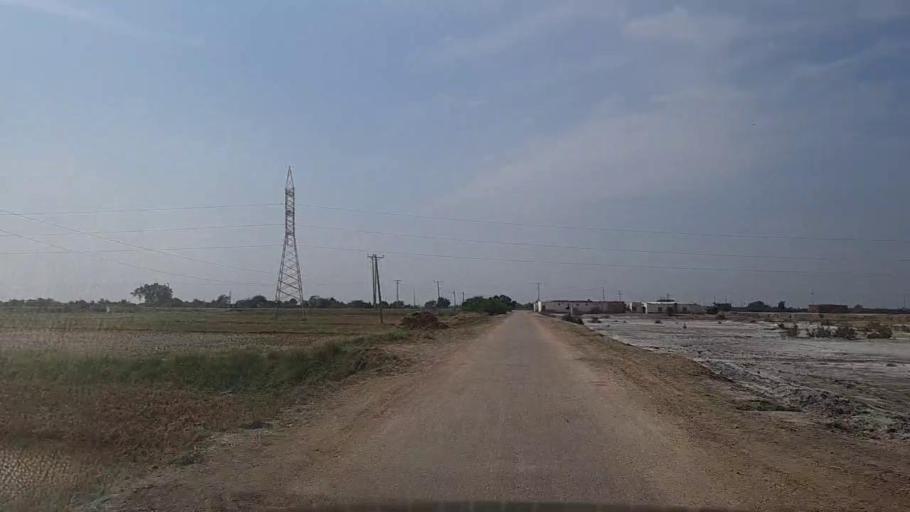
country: PK
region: Sindh
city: Thatta
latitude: 24.7874
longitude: 67.8662
